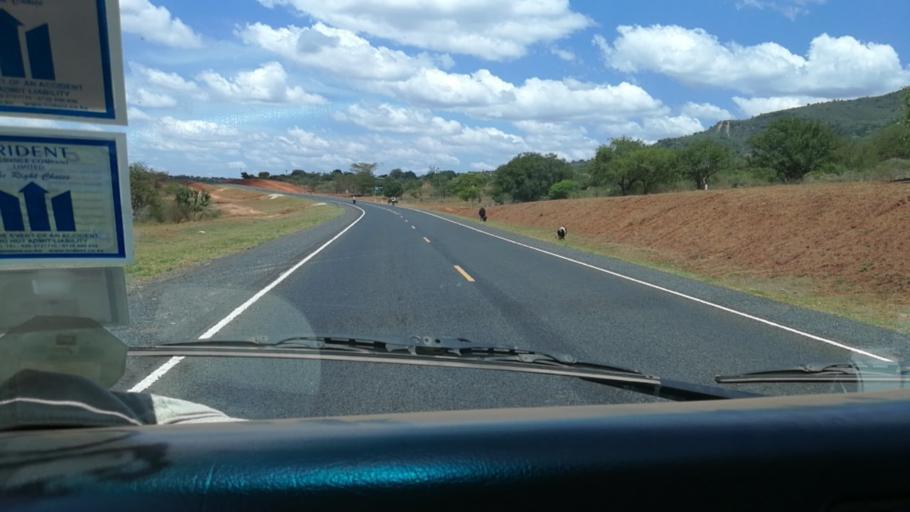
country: KE
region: Taita Taveta
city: Wundanyi
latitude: -3.5097
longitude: 38.3554
